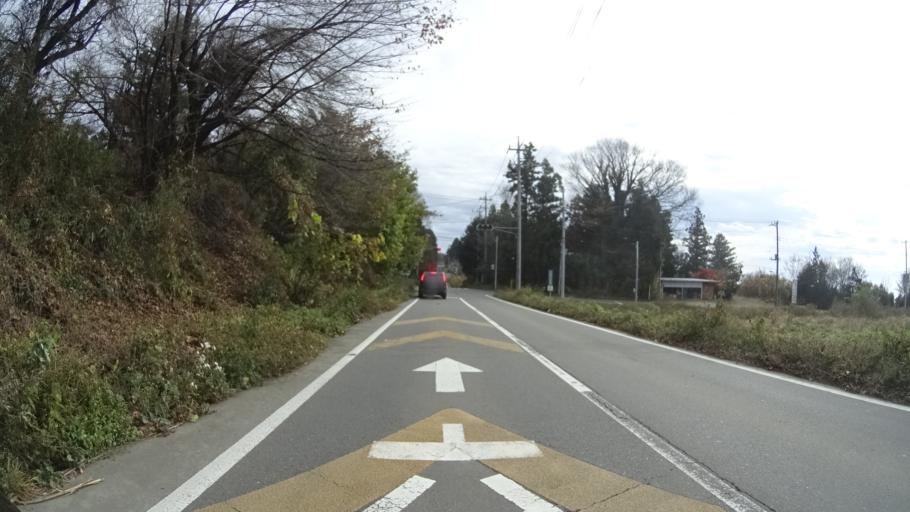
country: JP
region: Gunma
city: Shibukawa
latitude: 36.5223
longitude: 139.0683
